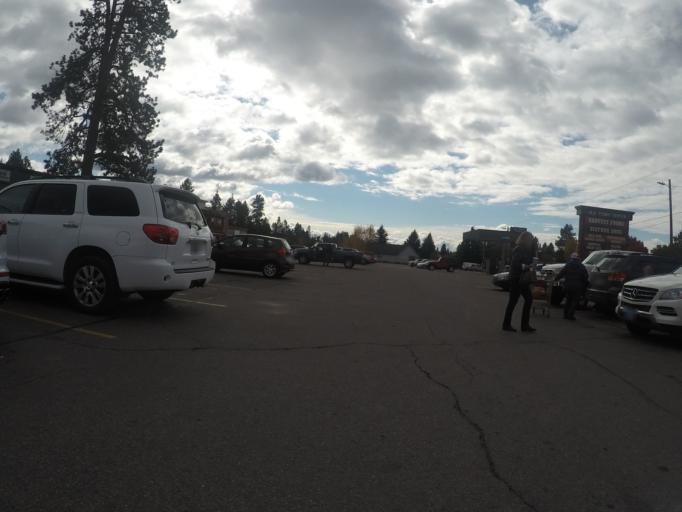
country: US
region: Montana
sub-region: Flathead County
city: Bigfork
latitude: 48.0731
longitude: -114.0786
